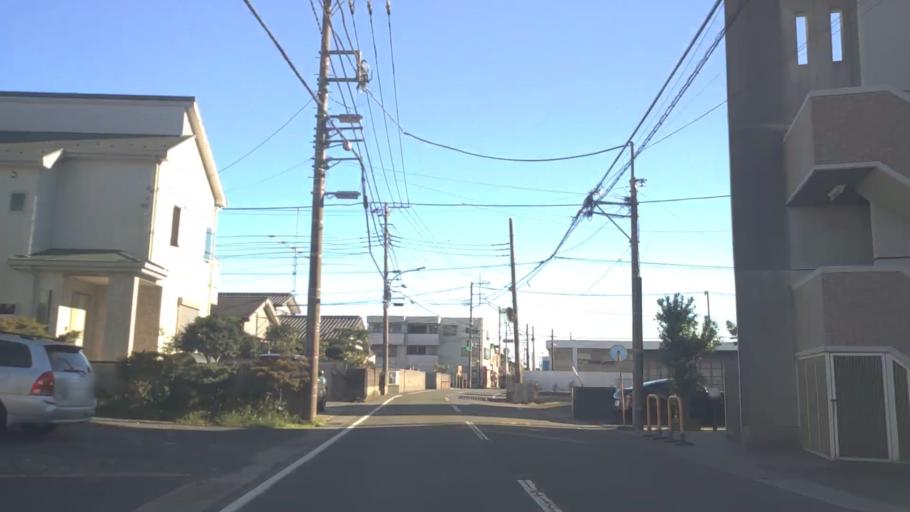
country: JP
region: Kanagawa
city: Isehara
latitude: 35.3809
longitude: 139.3648
